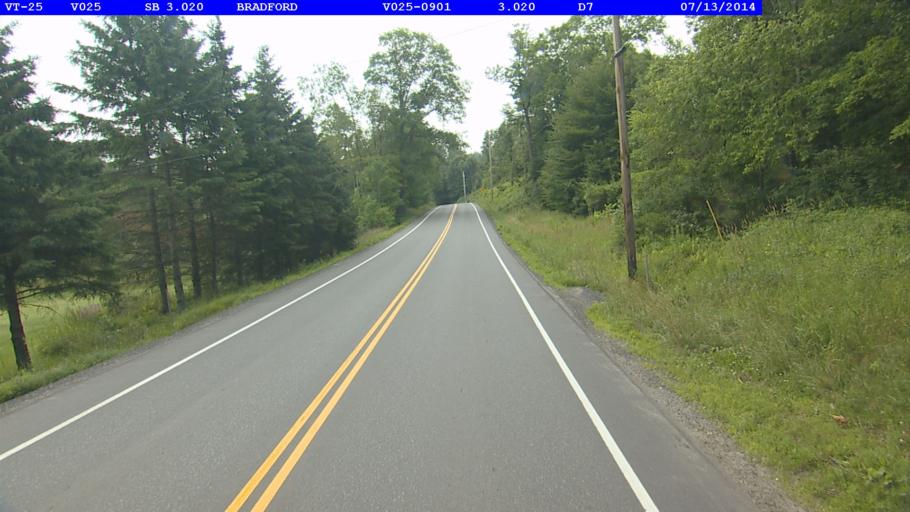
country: US
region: New Hampshire
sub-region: Grafton County
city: Orford
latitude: 43.9987
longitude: -72.1598
